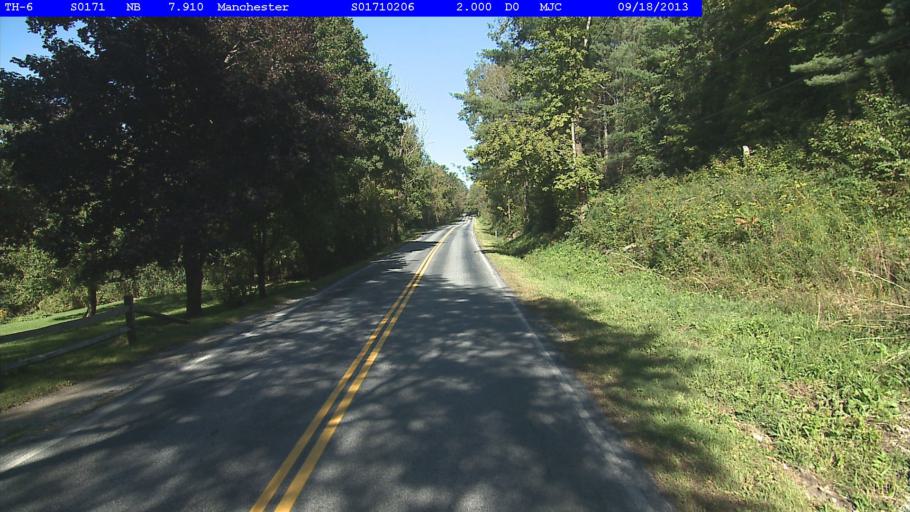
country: US
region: Vermont
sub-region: Bennington County
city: Manchester Center
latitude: 43.1371
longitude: -73.0658
